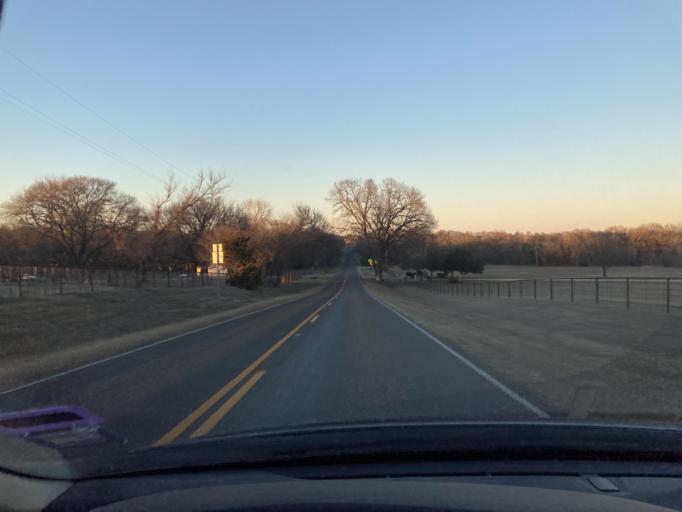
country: US
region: Texas
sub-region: Ellis County
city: Waxahachie
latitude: 32.3472
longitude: -96.8718
